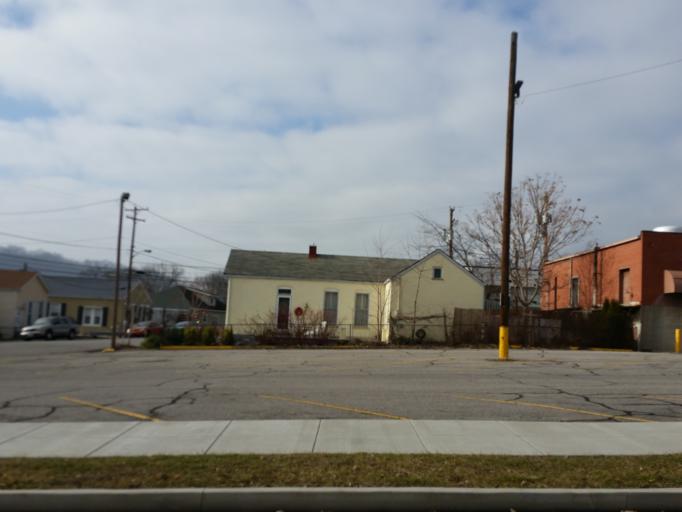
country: US
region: Indiana
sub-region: Jefferson County
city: Madison
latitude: 38.7344
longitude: -85.3787
